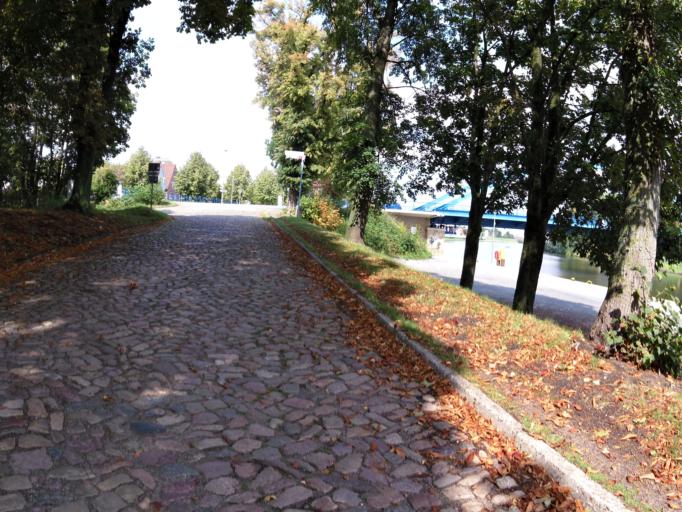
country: DE
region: Lower Saxony
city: Hoya
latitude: 52.8048
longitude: 9.1447
